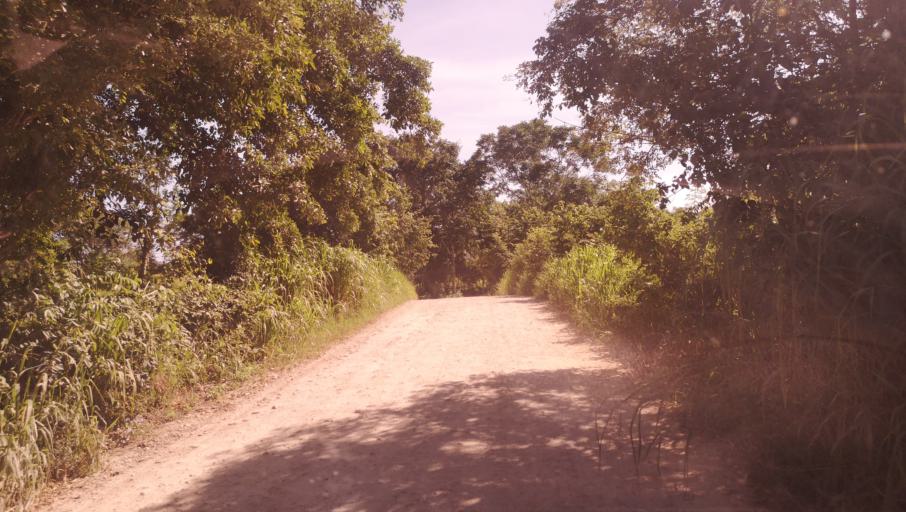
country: GT
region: Peten
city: Dolores
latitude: 16.7233
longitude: -89.3579
